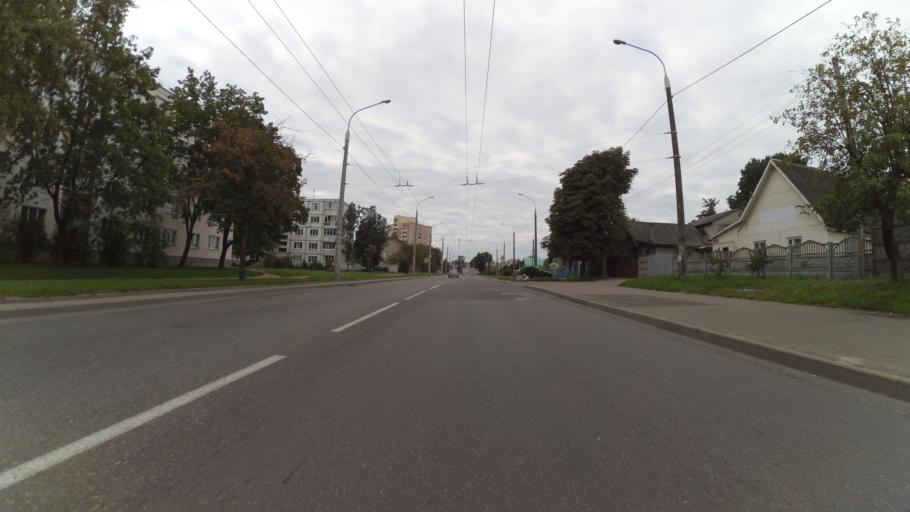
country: BY
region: Minsk
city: Vyaliki Trastsyanets
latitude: 53.8745
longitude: 27.6828
